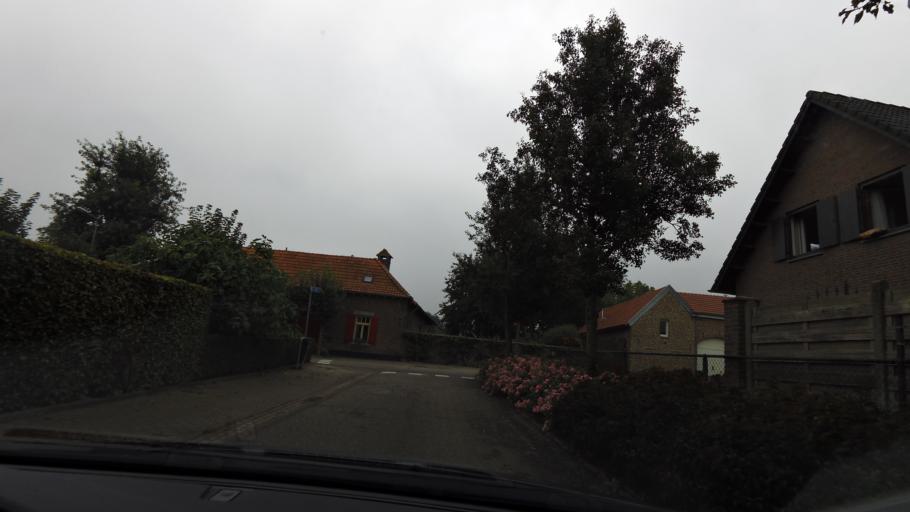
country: NL
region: Limburg
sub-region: Gemeente Onderbanken
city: Merkelbeek
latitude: 50.9677
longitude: 5.9396
